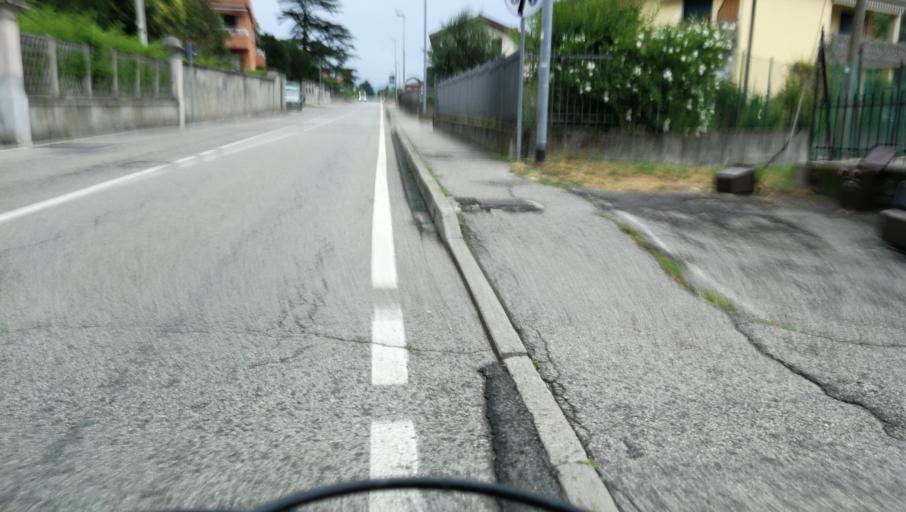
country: IT
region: Lombardy
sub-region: Provincia di Varese
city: Cittiglio
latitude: 45.8941
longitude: 8.6720
